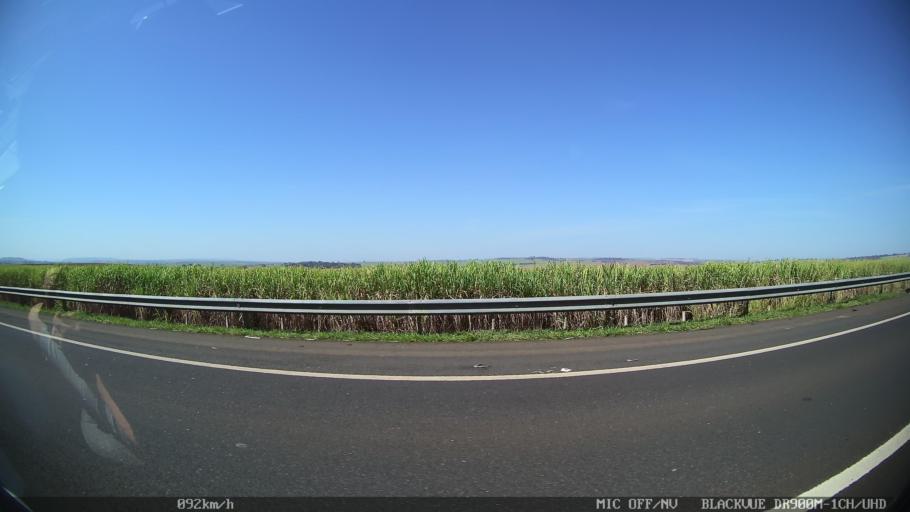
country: BR
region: Sao Paulo
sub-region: Batatais
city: Batatais
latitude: -20.7664
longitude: -47.5362
